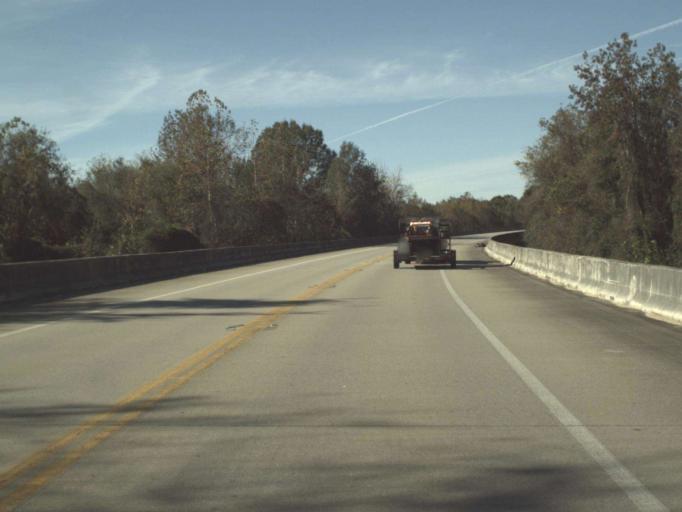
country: US
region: Florida
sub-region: Escambia County
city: Century
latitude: 30.9586
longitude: -87.2316
